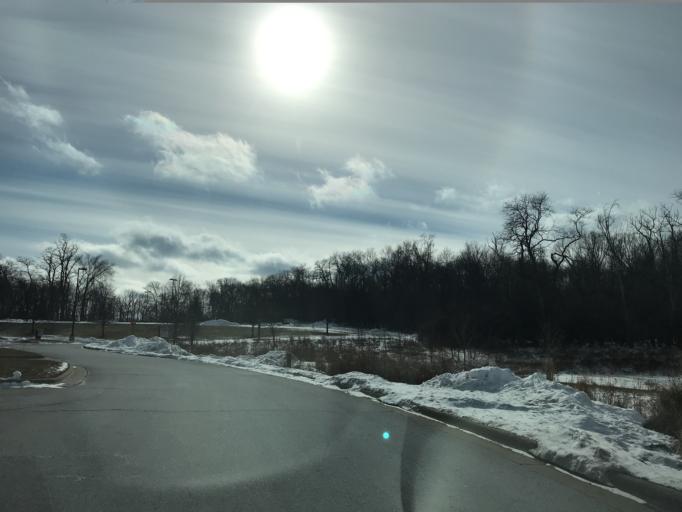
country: US
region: Michigan
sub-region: Washtenaw County
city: Ypsilanti
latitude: 42.2631
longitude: -83.6690
